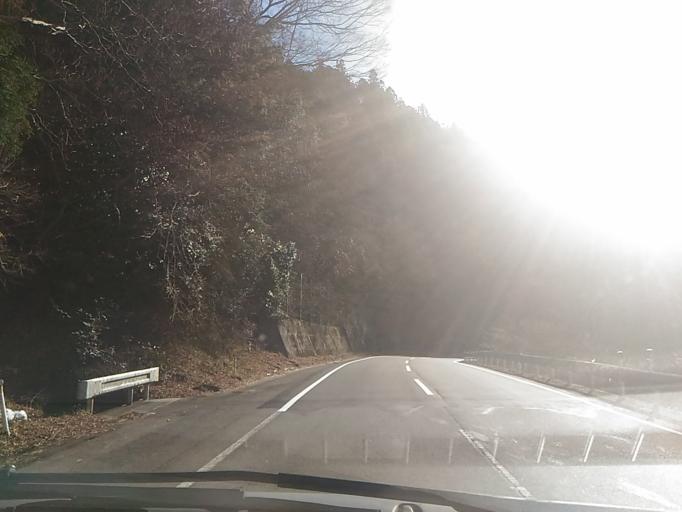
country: JP
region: Fukushima
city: Iwaki
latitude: 37.0233
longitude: 140.6626
